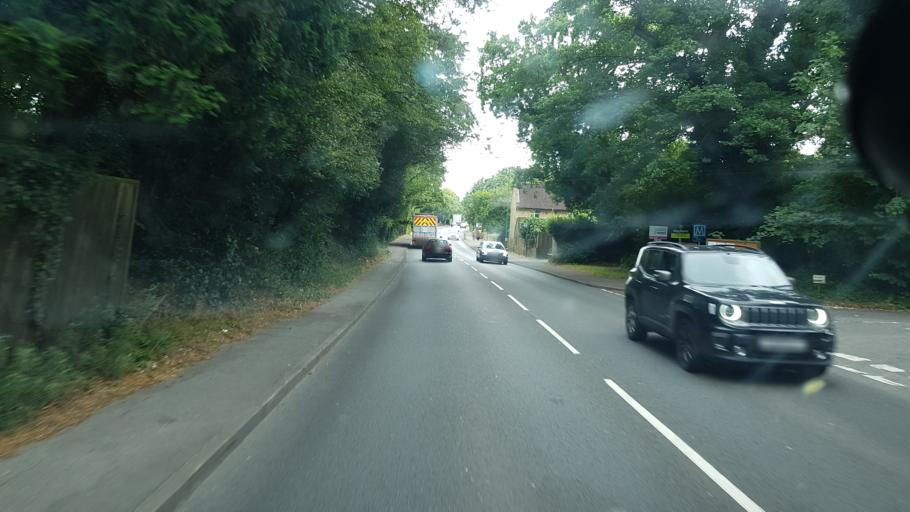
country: GB
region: England
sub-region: Surrey
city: Lingfield
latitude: 51.1972
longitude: -0.0538
